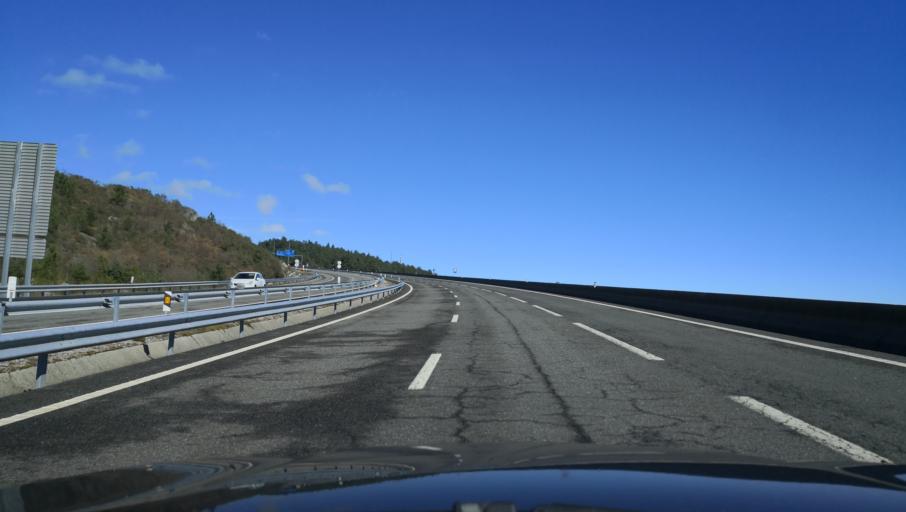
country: PT
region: Vila Real
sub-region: Vila Pouca de Aguiar
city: Vila Pouca de Aguiar
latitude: 41.4963
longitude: -7.6561
